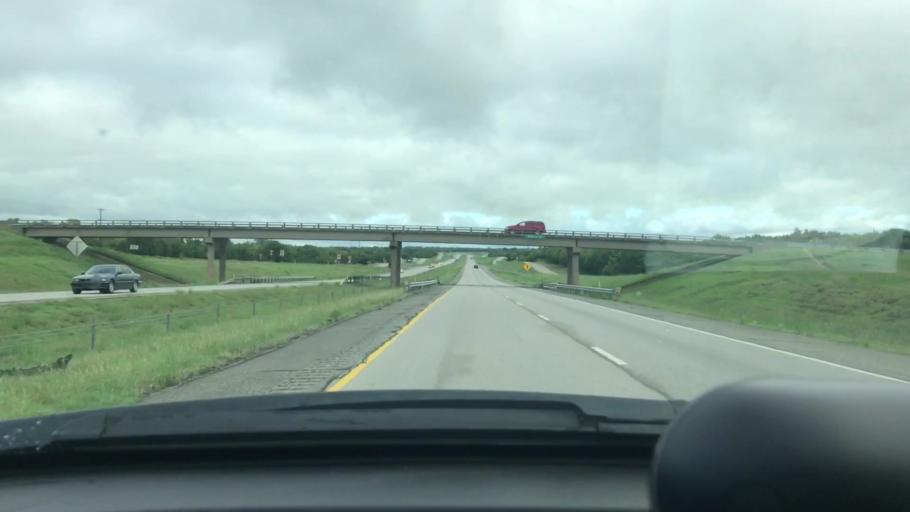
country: US
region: Texas
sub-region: Grayson County
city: Van Alstyne
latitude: 33.3810
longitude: -96.5807
